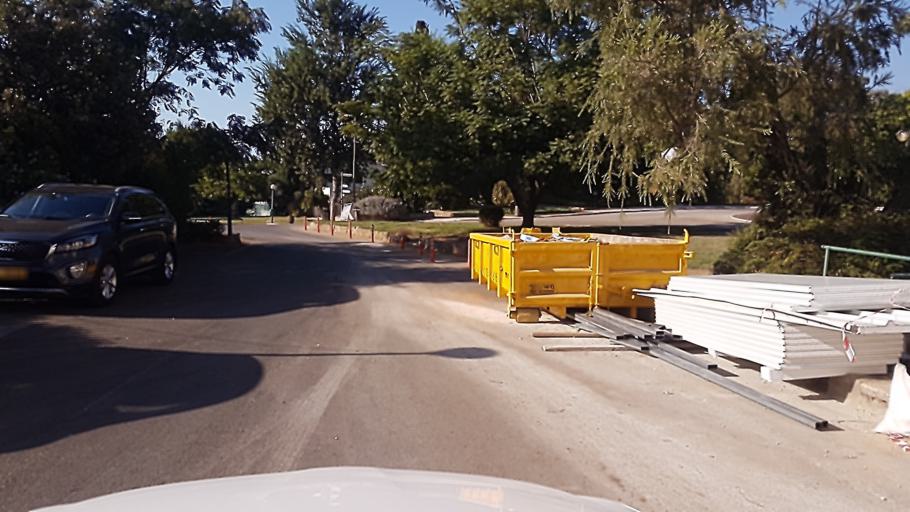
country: IL
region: Central District
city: Kfar Saba
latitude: 32.2005
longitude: 34.9257
